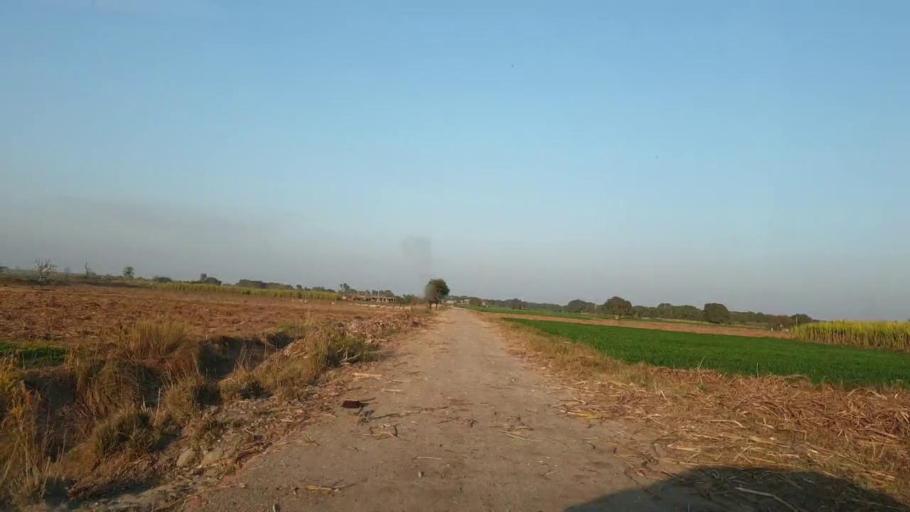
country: PK
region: Sindh
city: Tando Jam
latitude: 25.4782
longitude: 68.5999
